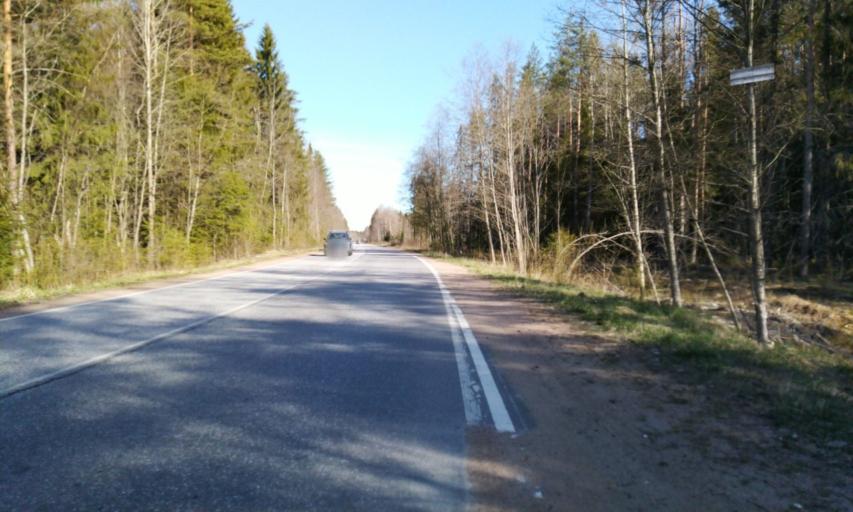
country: RU
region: Leningrad
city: Garbolovo
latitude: 60.3302
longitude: 30.4434
